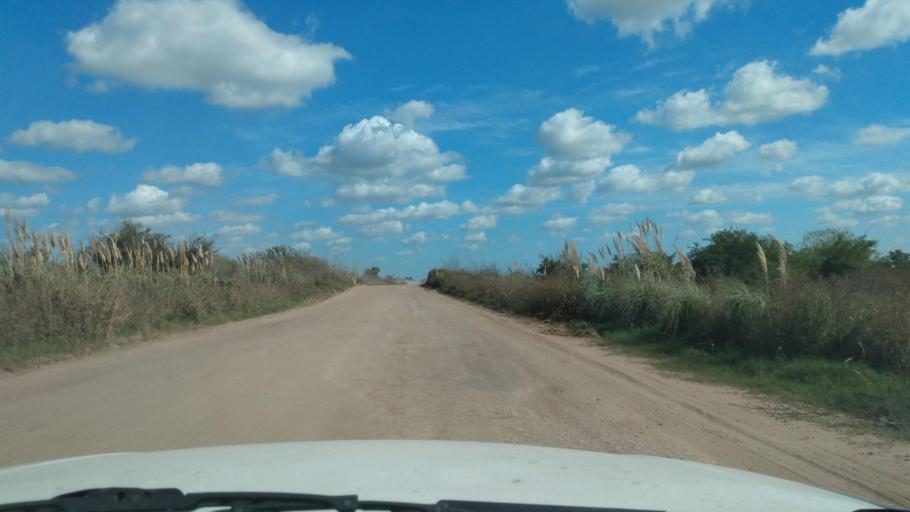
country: AR
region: Buenos Aires
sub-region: Partido de Navarro
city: Navarro
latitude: -35.0019
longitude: -59.3541
